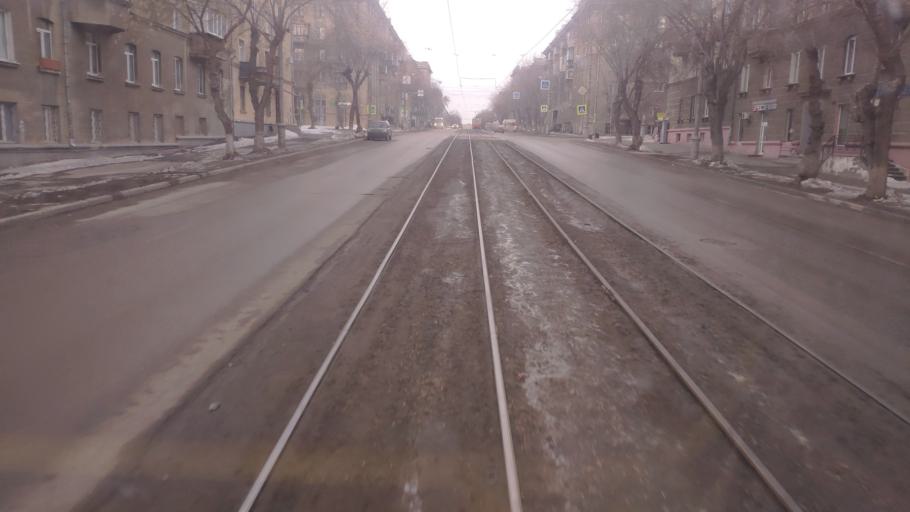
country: RU
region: Chelyabinsk
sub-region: Gorod Magnitogorsk
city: Magnitogorsk
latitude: 53.4200
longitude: 58.9990
